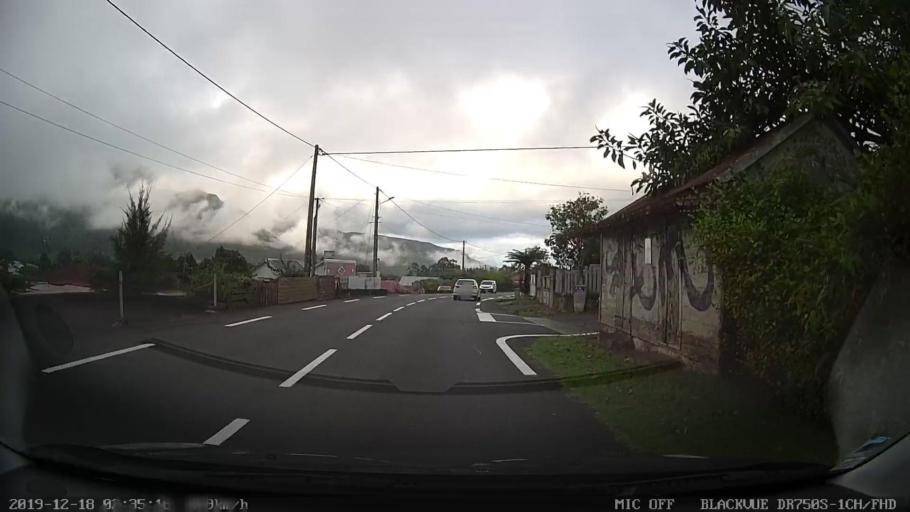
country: RE
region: Reunion
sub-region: Reunion
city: Salazie
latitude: -21.1480
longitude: 55.6159
